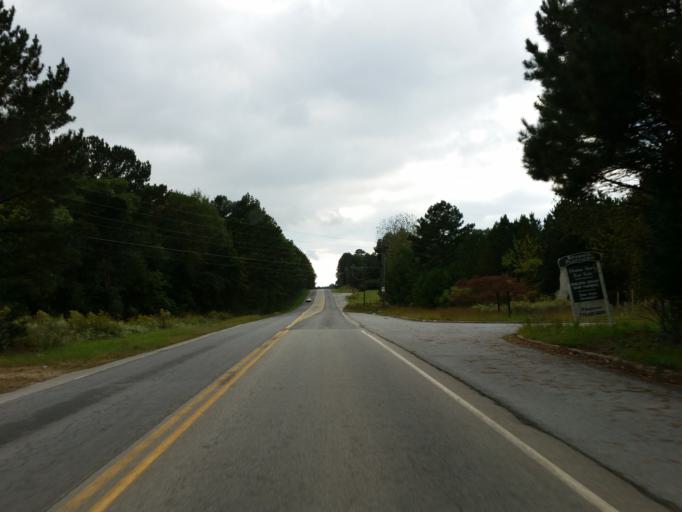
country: US
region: Georgia
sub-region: Bartow County
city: Cartersville
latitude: 34.1170
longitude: -84.8264
